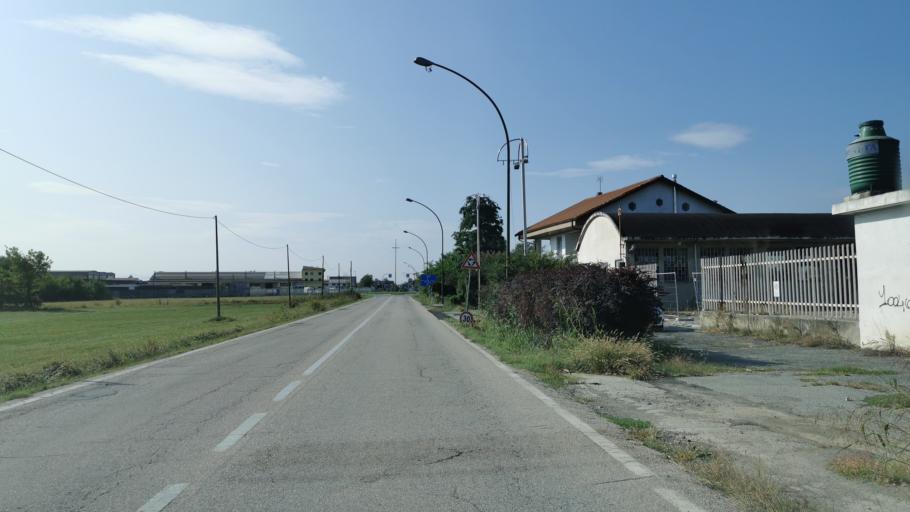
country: IT
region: Piedmont
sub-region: Provincia di Torino
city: Leini
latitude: 45.2043
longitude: 7.7270
